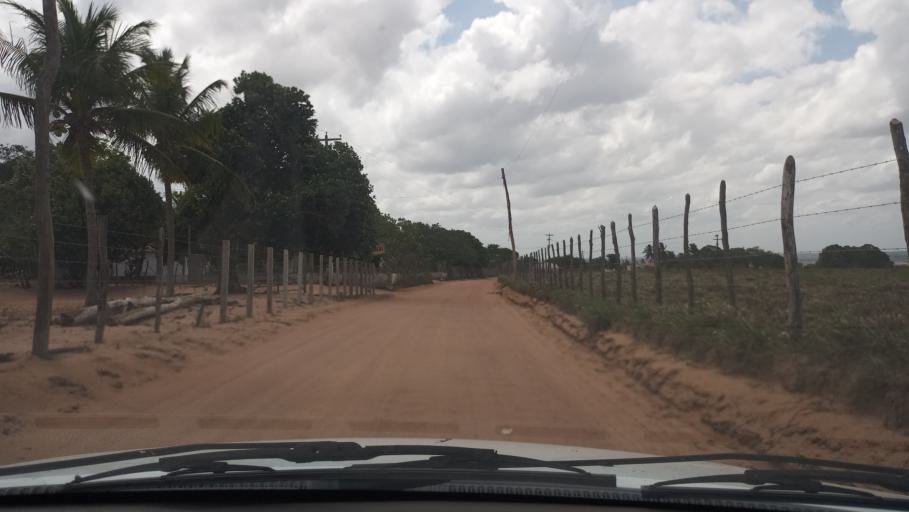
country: BR
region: Rio Grande do Norte
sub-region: Montanhas
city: Montanhas
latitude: -6.3597
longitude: -35.3361
